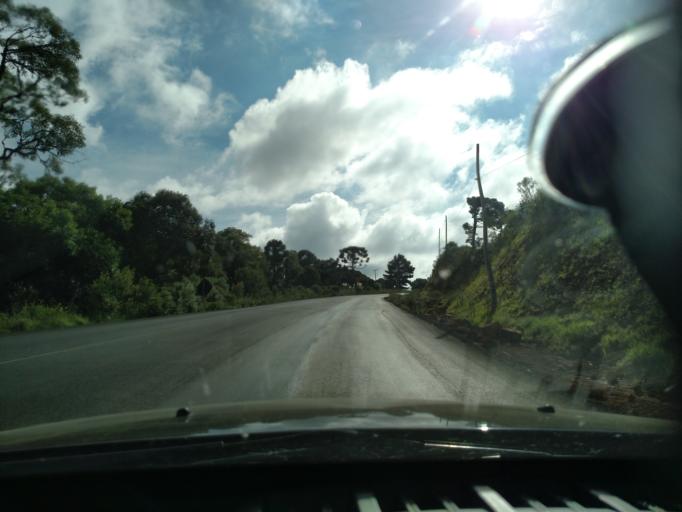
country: BR
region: Rio Grande do Sul
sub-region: Vacaria
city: Estrela
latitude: -27.9182
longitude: -50.6599
